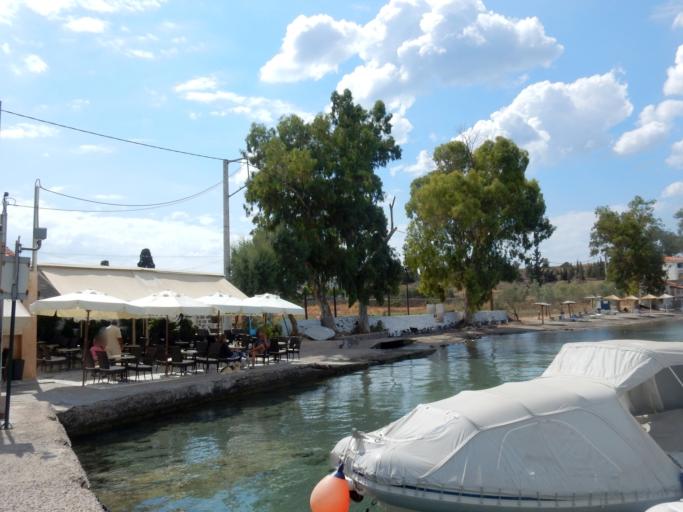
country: GR
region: Attica
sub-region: Nomos Piraios
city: Aegina
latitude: 37.6910
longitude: 23.4541
